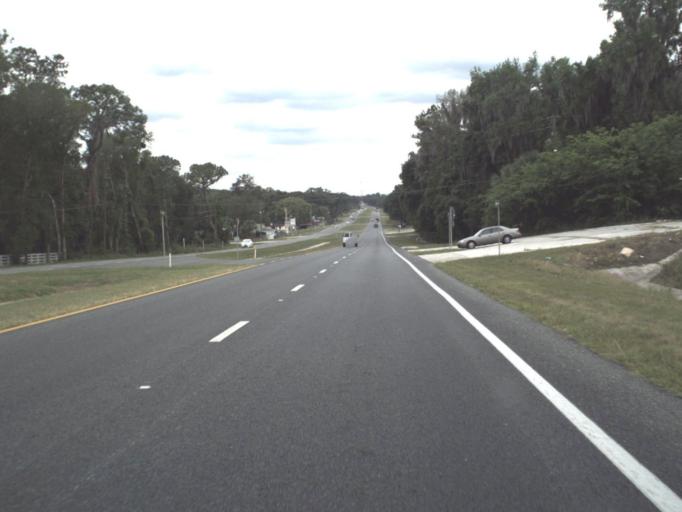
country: US
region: Florida
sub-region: Marion County
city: Citra
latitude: 29.4326
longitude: -82.2215
